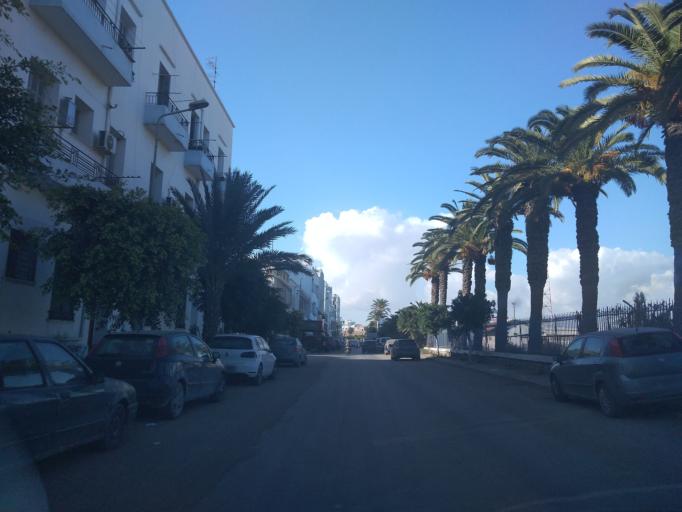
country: TN
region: Safaqis
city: Sfax
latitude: 34.7330
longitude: 10.7681
